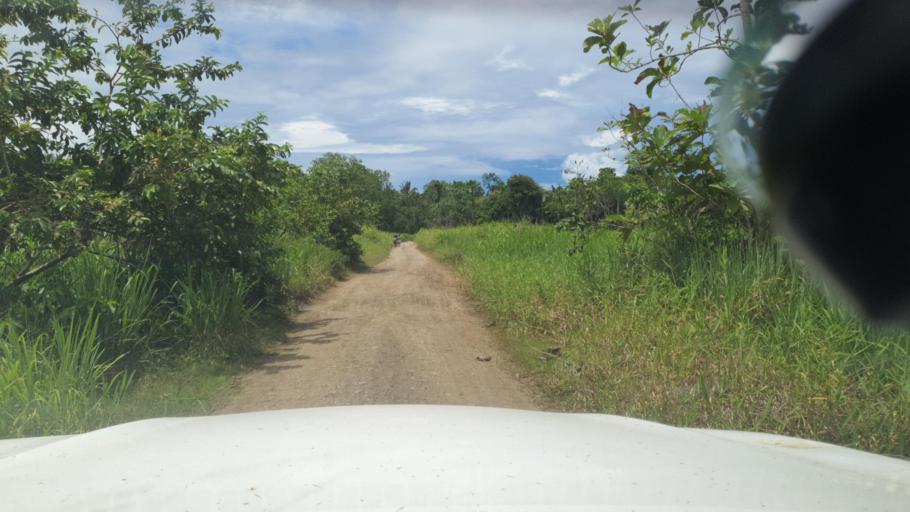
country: SB
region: Guadalcanal
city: Honiara
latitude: -9.4878
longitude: 160.3409
